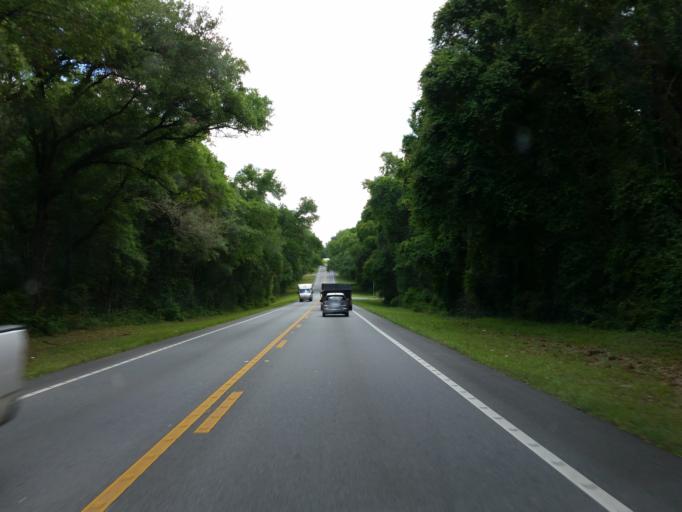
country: US
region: Florida
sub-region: Citrus County
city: Hernando
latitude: 28.9334
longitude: -82.3955
